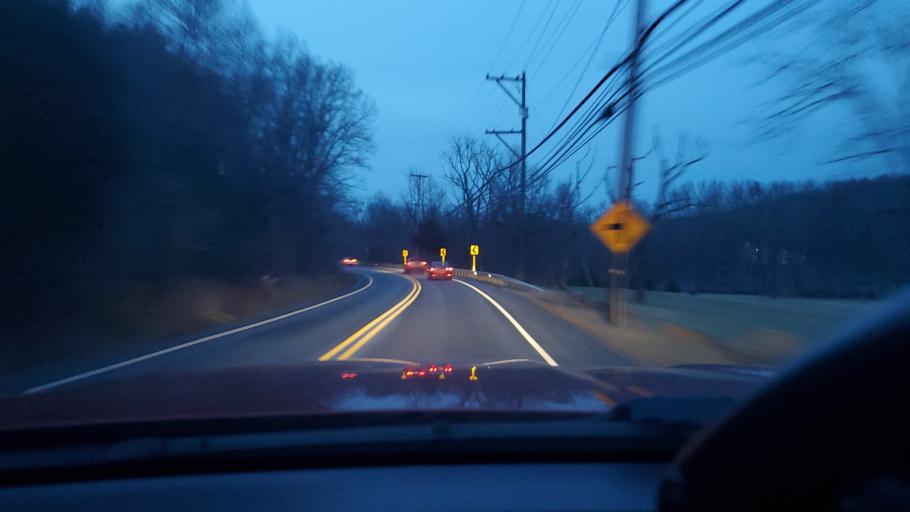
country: US
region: Pennsylvania
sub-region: Montgomery County
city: Spring Mount
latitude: 40.2706
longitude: -75.4713
